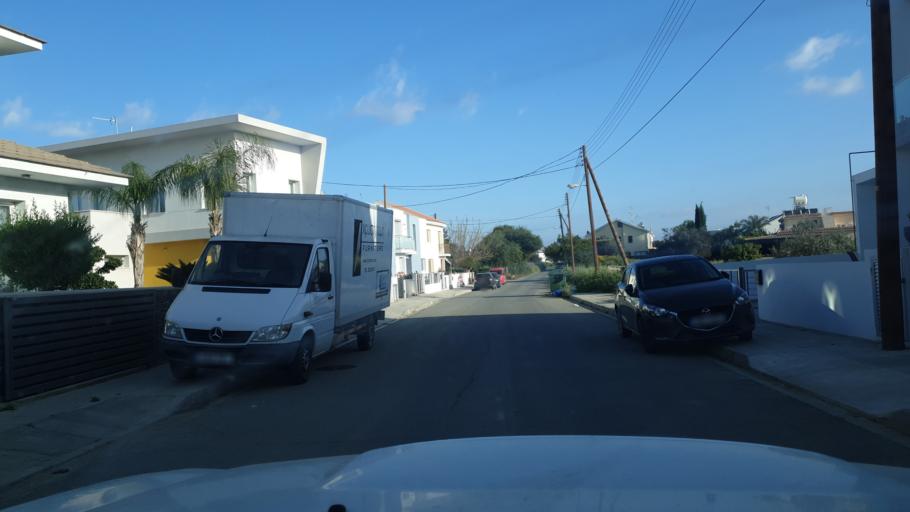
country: CY
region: Lefkosia
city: Tseri
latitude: 35.0642
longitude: 33.3270
